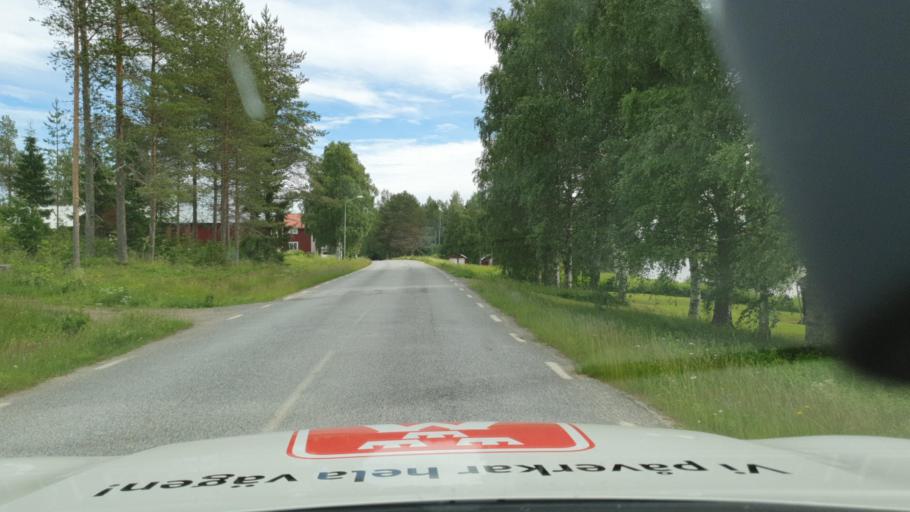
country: SE
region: Vaesterbotten
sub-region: Skelleftea Kommun
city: Soedra Bergsbyn
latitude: 64.5099
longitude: 21.0012
